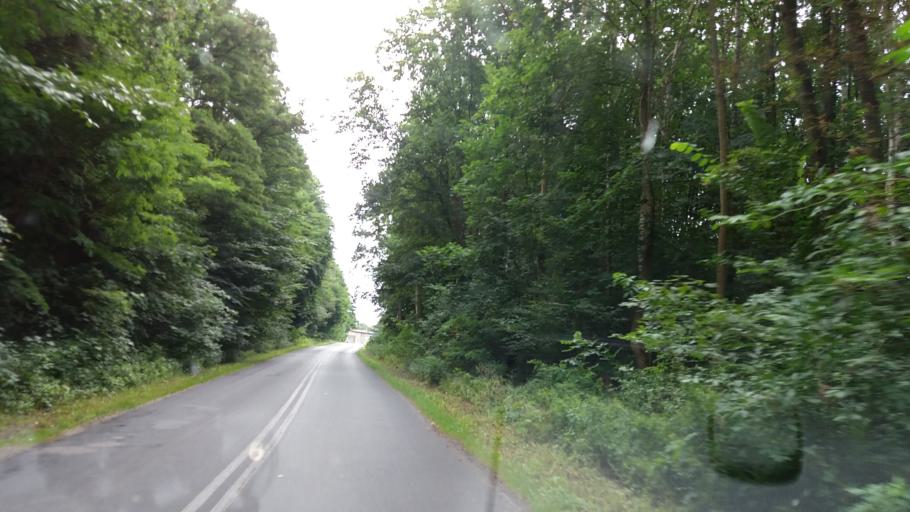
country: PL
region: West Pomeranian Voivodeship
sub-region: Powiat choszczenski
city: Krzecin
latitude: 53.0864
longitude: 15.4774
